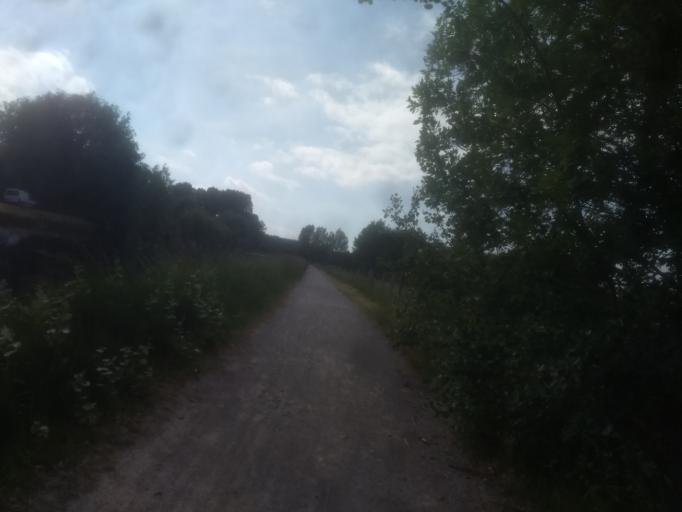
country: FR
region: Nord-Pas-de-Calais
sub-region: Departement du Pas-de-Calais
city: Feuchy
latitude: 50.2992
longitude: 2.8354
